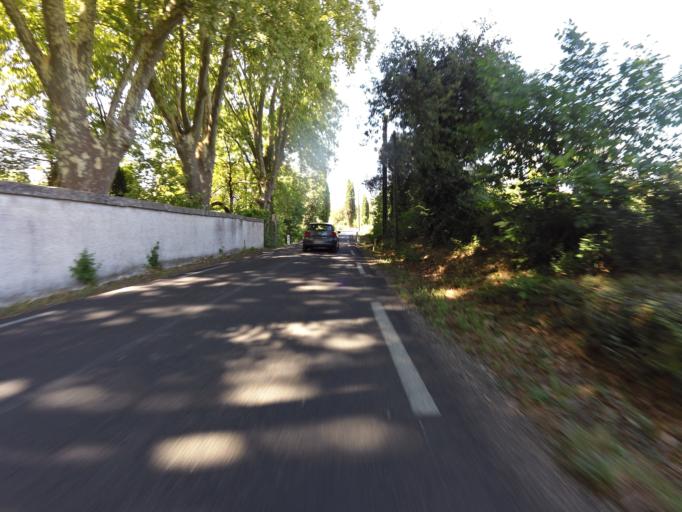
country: FR
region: Languedoc-Roussillon
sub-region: Departement de l'Herault
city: Boisseron
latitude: 43.7625
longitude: 4.1017
